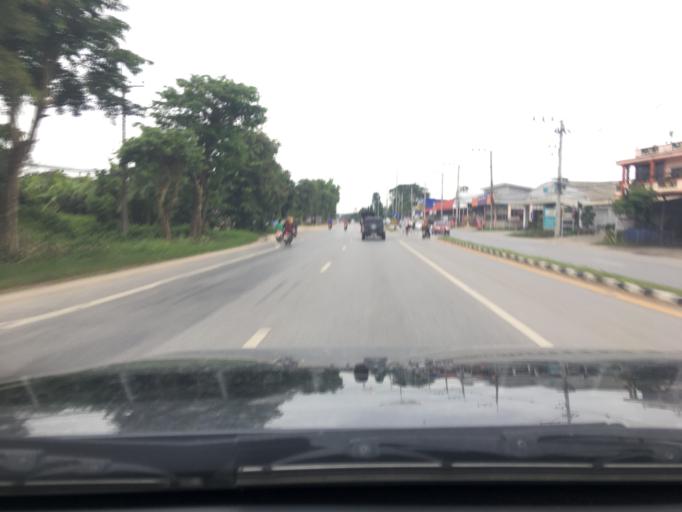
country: TH
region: Chiang Rai
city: Chiang Rai
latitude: 19.9511
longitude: 99.8492
